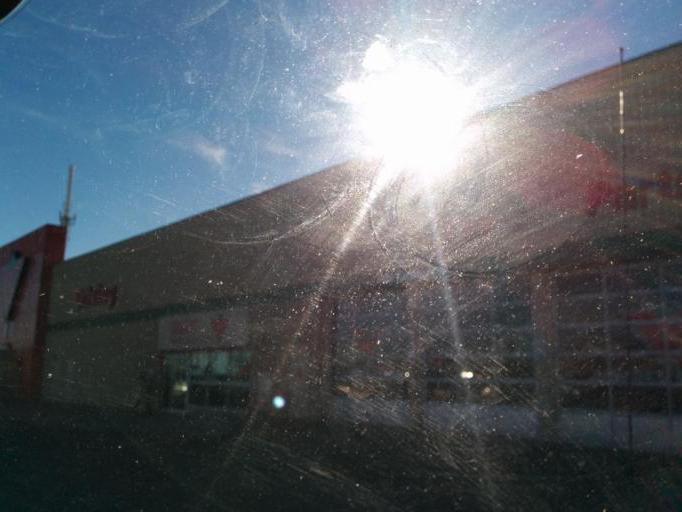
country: CA
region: Ontario
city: Mississauga
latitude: 43.5666
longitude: -79.6358
